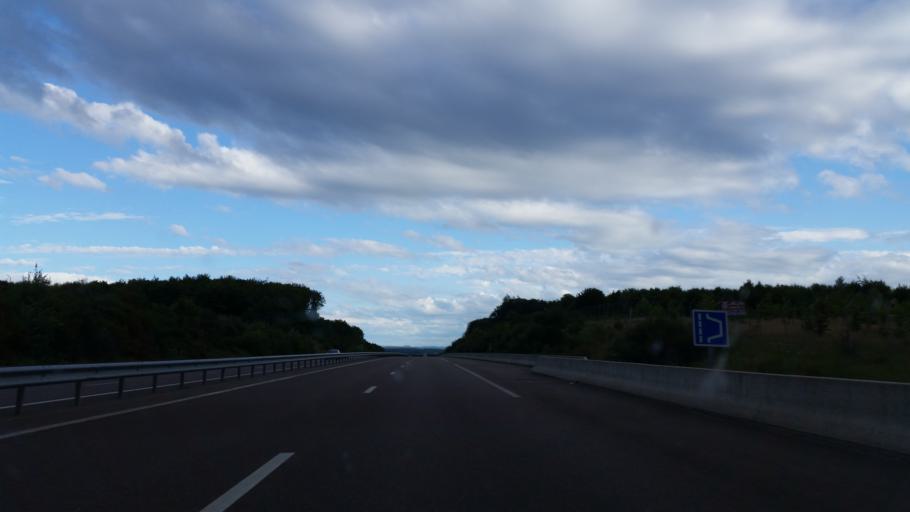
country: FR
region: Franche-Comte
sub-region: Departement de la Haute-Saone
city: Froideconche
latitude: 47.8478
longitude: 6.3890
